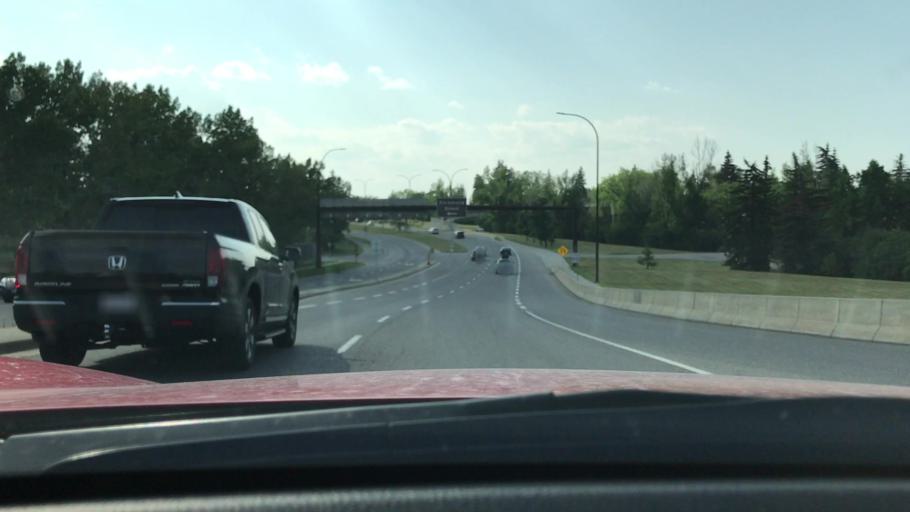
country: CA
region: Alberta
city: Calgary
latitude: 51.0241
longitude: -114.1191
